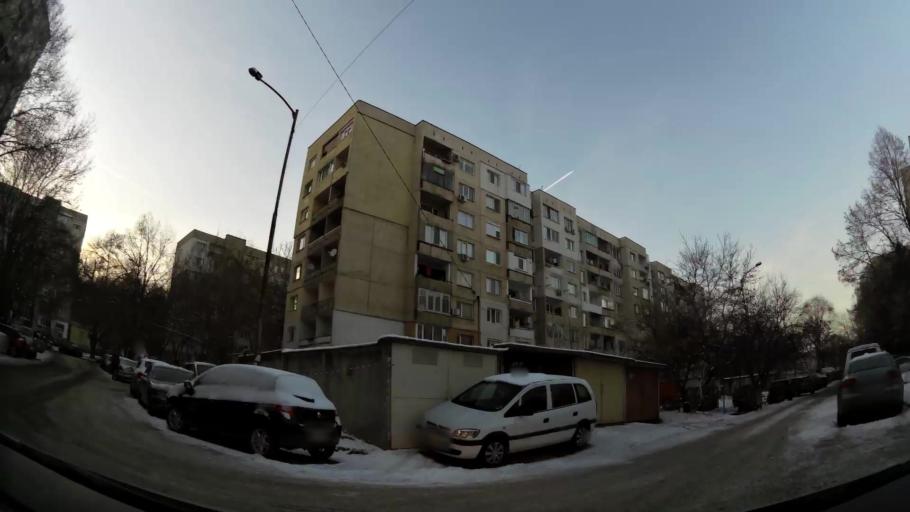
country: BG
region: Sofia-Capital
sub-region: Stolichna Obshtina
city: Sofia
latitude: 42.6834
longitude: 23.3730
